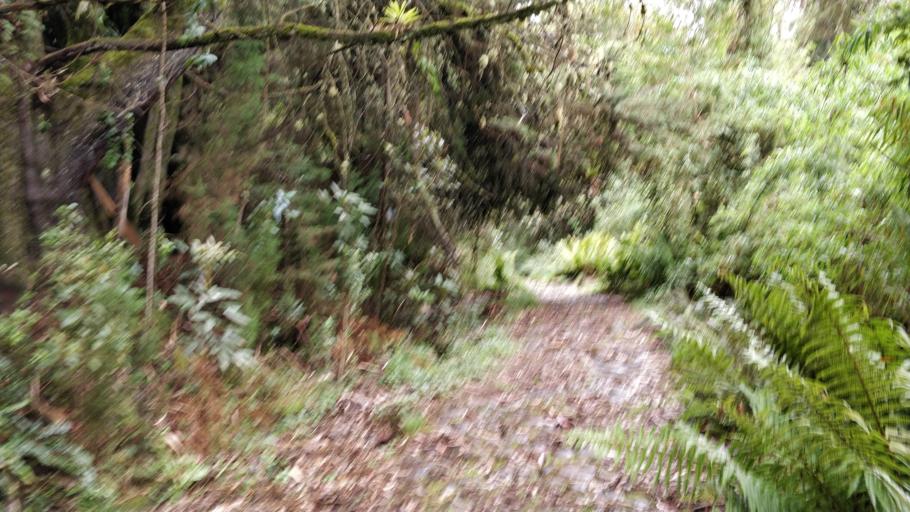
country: CO
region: Bogota D.C.
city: Bogota
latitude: 4.5413
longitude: -74.0541
